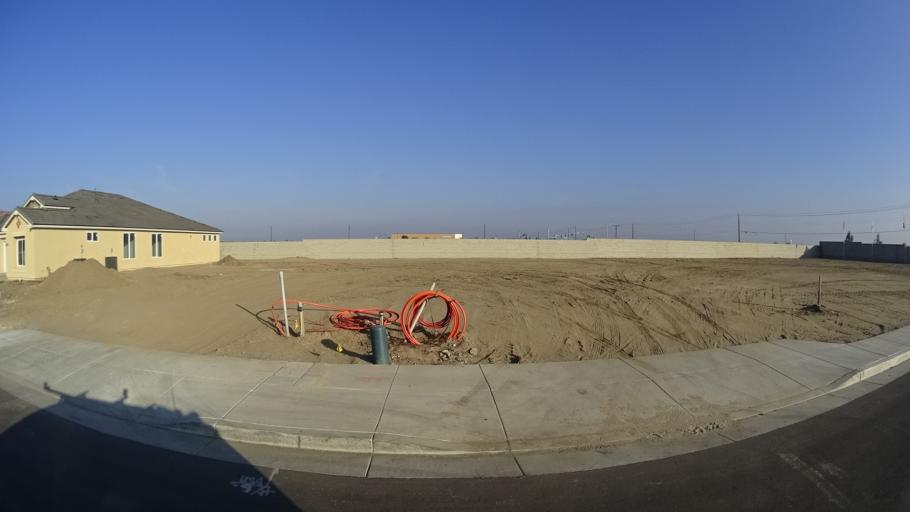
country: US
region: California
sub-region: Kern County
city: Greenacres
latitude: 35.2938
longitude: -119.1107
